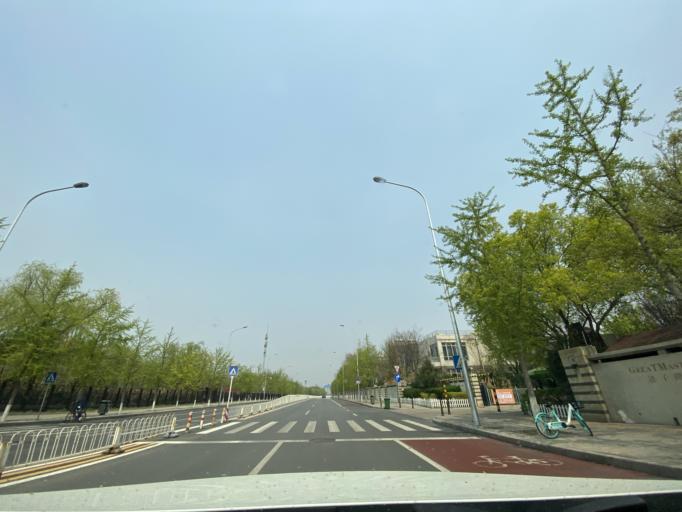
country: CN
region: Beijing
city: Sijiqing
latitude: 39.9420
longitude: 116.2621
